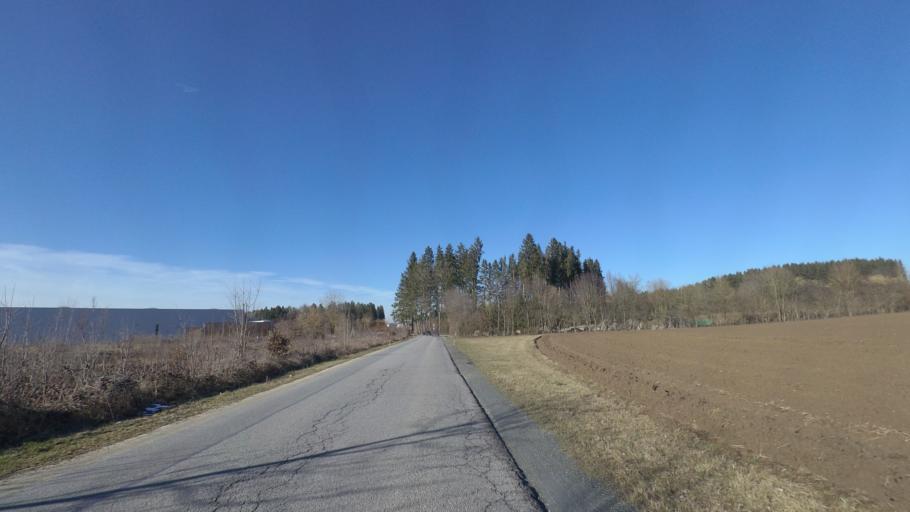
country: DE
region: Bavaria
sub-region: Upper Bavaria
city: Traunreut
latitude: 47.9534
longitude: 12.6189
